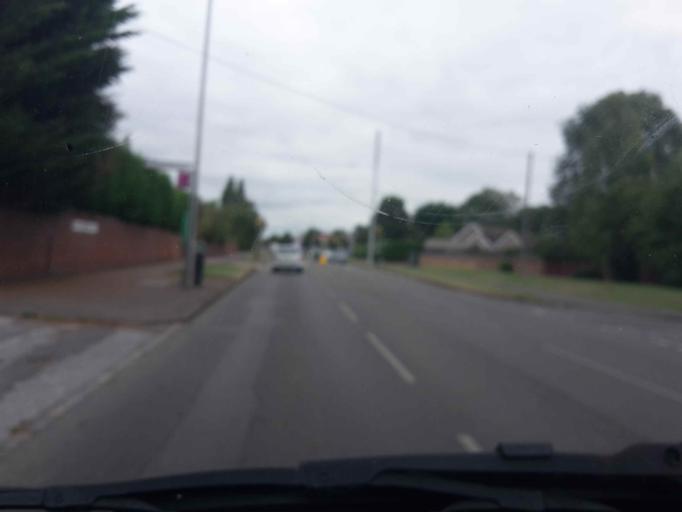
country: GB
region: England
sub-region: Reading
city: Reading
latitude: 51.4769
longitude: -0.9667
